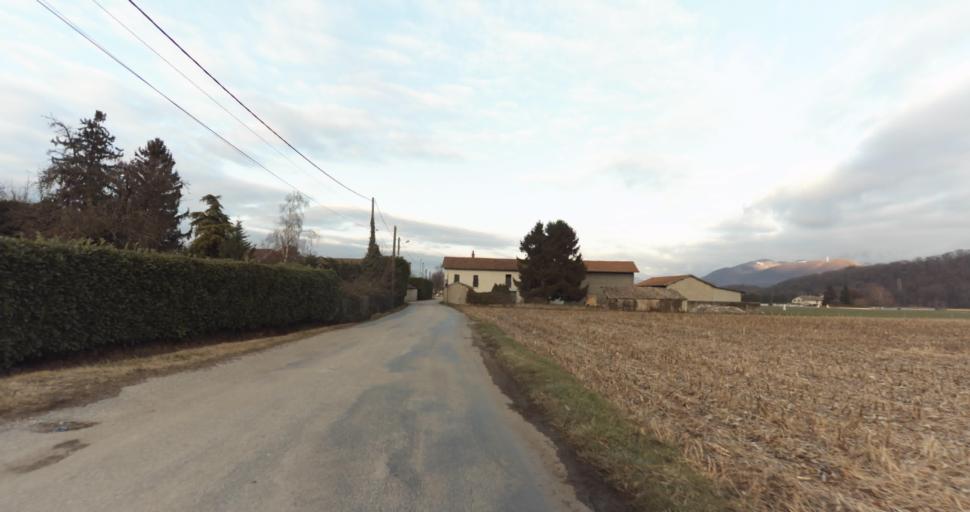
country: FR
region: Rhone-Alpes
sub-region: Departement de l'Isere
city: Vif
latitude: 45.0760
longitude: 5.7006
